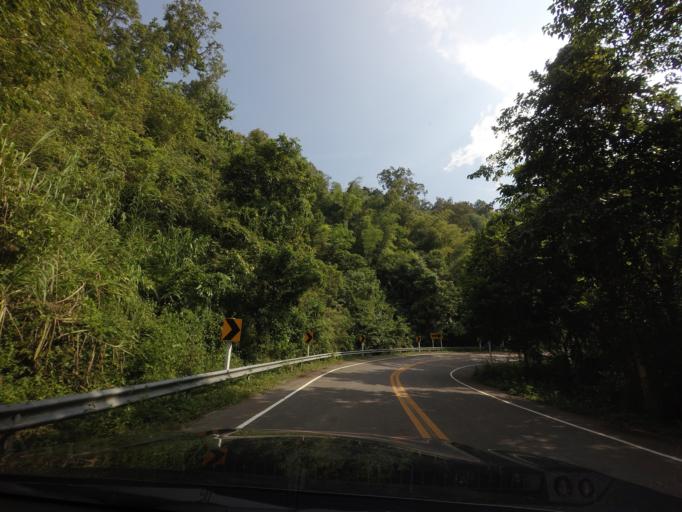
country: TH
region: Nan
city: Na Noi
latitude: 18.2856
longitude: 100.9318
